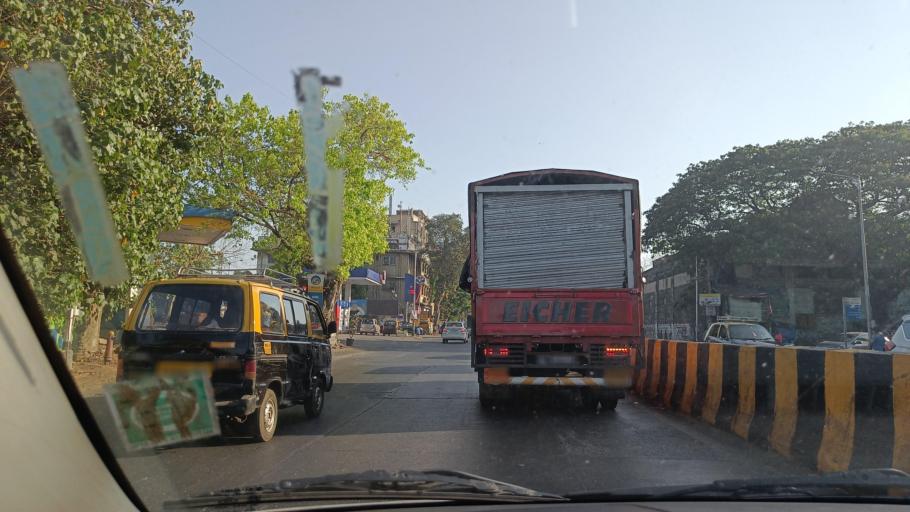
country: IN
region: Maharashtra
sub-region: Raigarh
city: Uran
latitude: 18.9533
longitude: 72.8417
